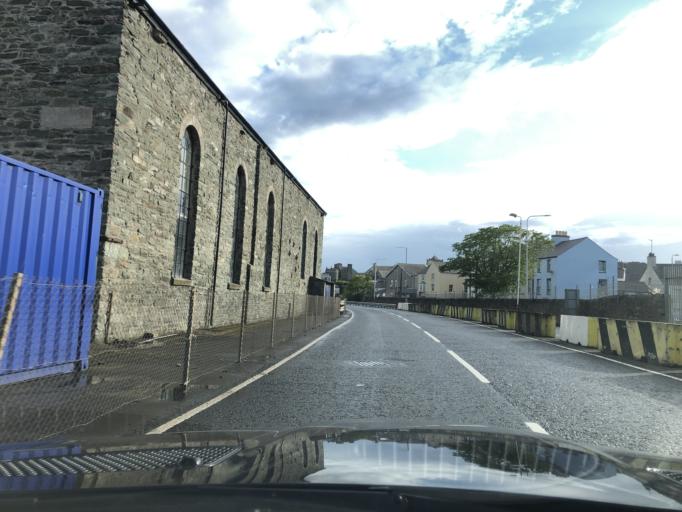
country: GB
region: Wales
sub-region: Anglesey
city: Holyhead
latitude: 53.3131
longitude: -4.6298
